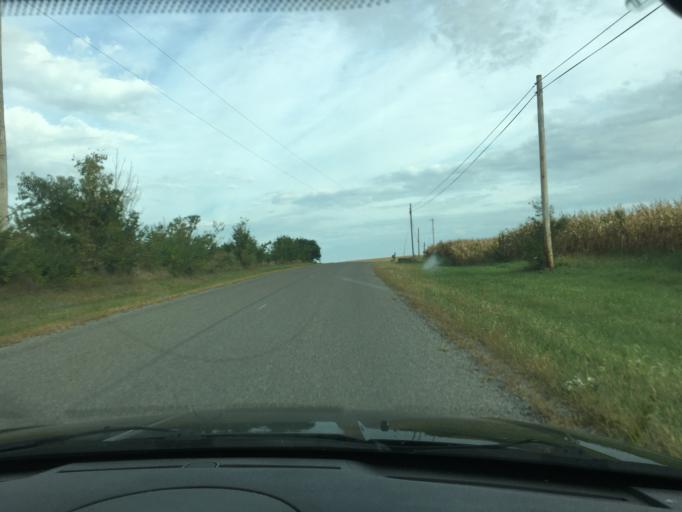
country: US
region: Ohio
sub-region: Logan County
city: West Liberty
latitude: 40.3006
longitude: -83.6874
